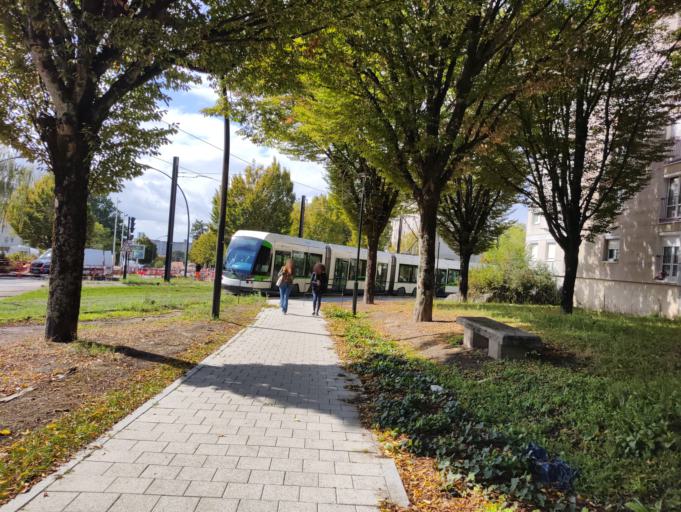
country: FR
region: Pays de la Loire
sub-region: Departement de la Loire-Atlantique
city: Bouguenais
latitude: 47.2047
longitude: -1.6033
